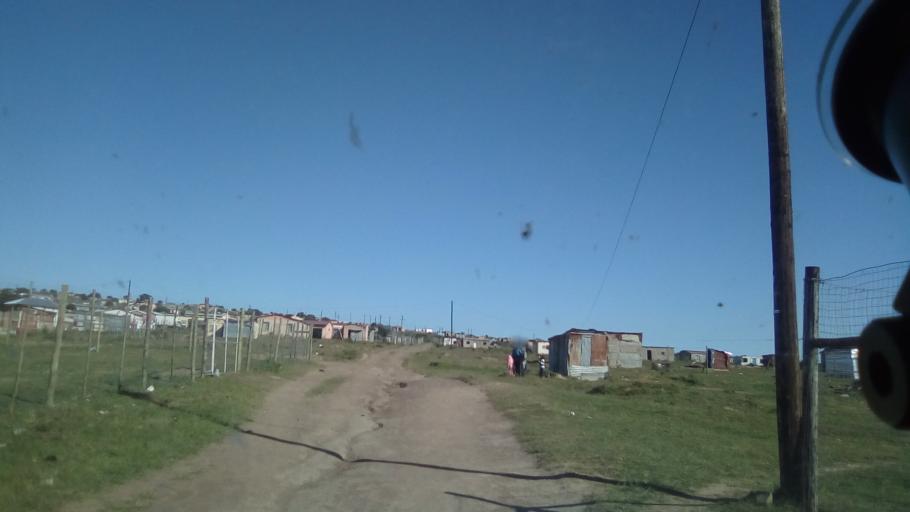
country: ZA
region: Eastern Cape
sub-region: Buffalo City Metropolitan Municipality
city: Bhisho
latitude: -32.8299
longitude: 27.3676
